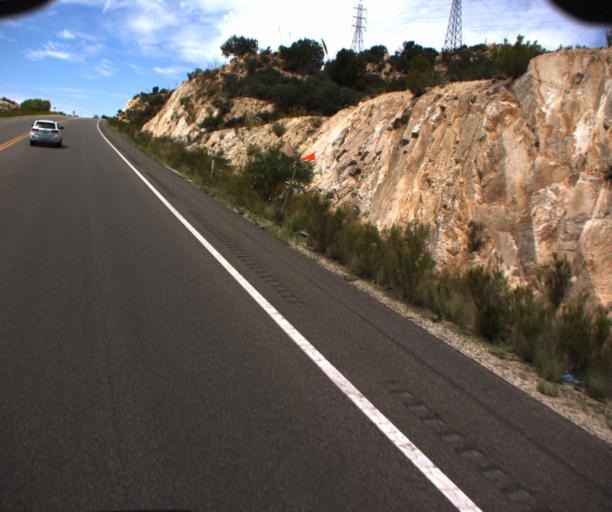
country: US
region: Arizona
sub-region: Gila County
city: Miami
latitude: 33.3688
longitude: -110.9344
